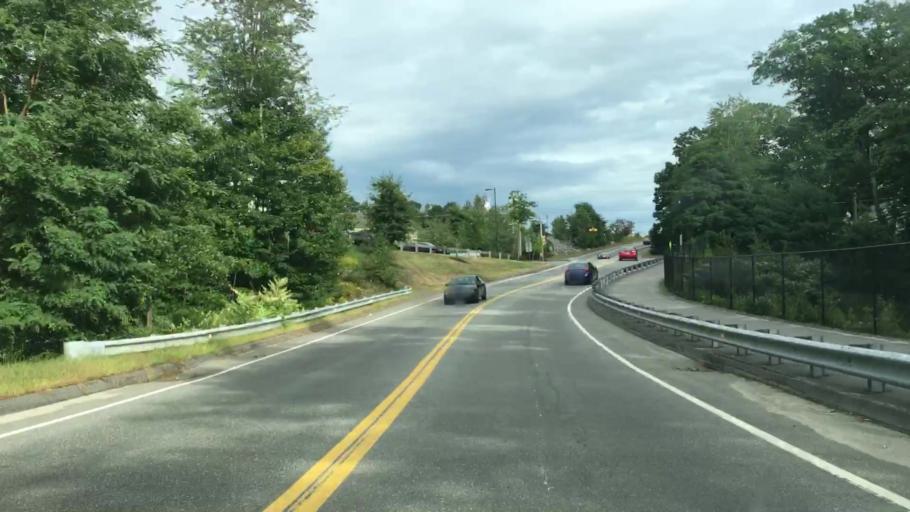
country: US
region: Maine
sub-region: Sagadahoc County
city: Topsham
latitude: 43.9378
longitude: -69.9753
